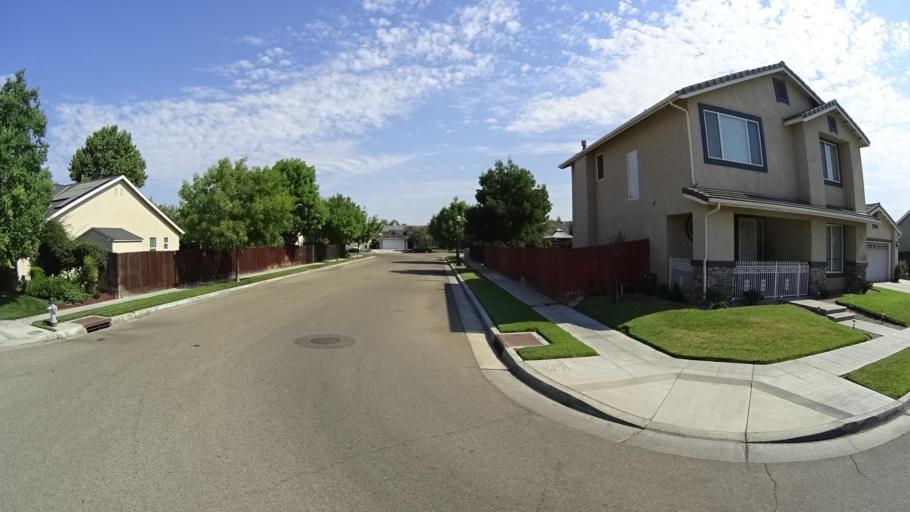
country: US
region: California
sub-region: Fresno County
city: Sunnyside
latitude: 36.7087
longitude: -119.6896
